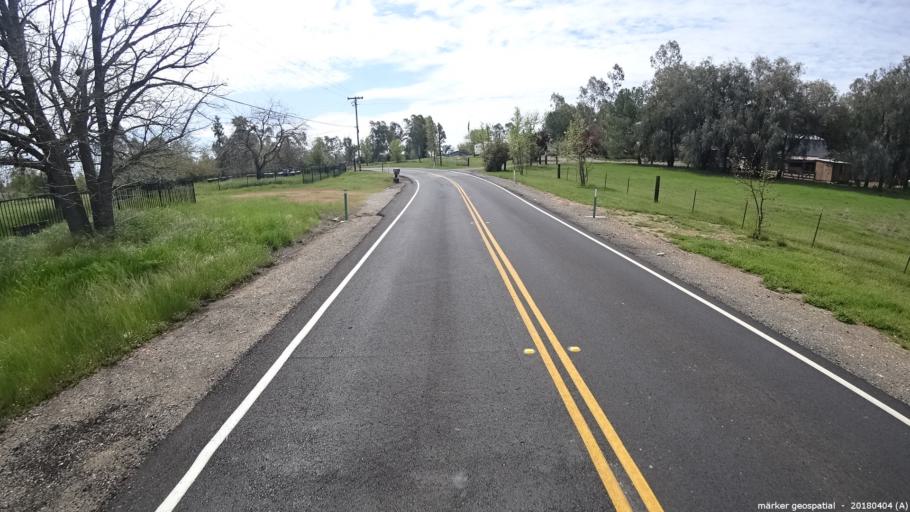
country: US
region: California
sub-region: Sacramento County
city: Clay
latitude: 38.3310
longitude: -121.1598
